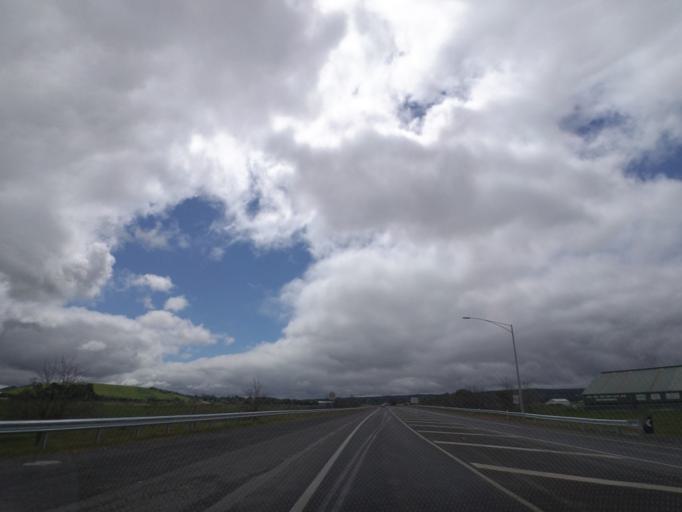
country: AU
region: Victoria
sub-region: Ballarat North
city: Lake Wendouree
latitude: -37.5175
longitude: 143.8451
